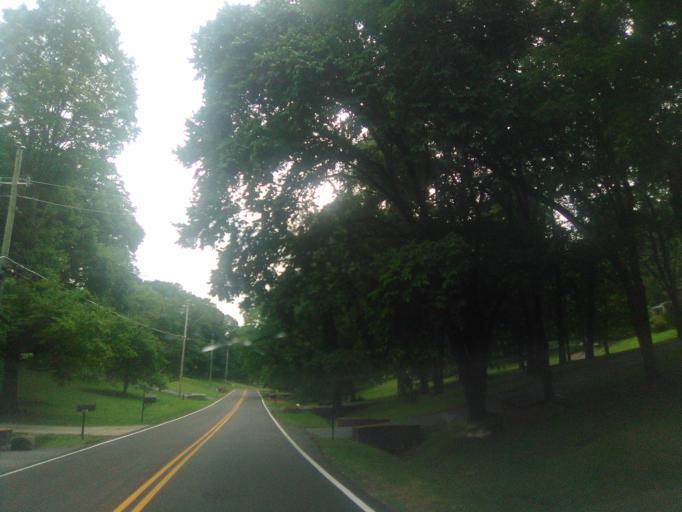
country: US
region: Tennessee
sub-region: Davidson County
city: Forest Hills
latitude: 36.0676
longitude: -86.8548
